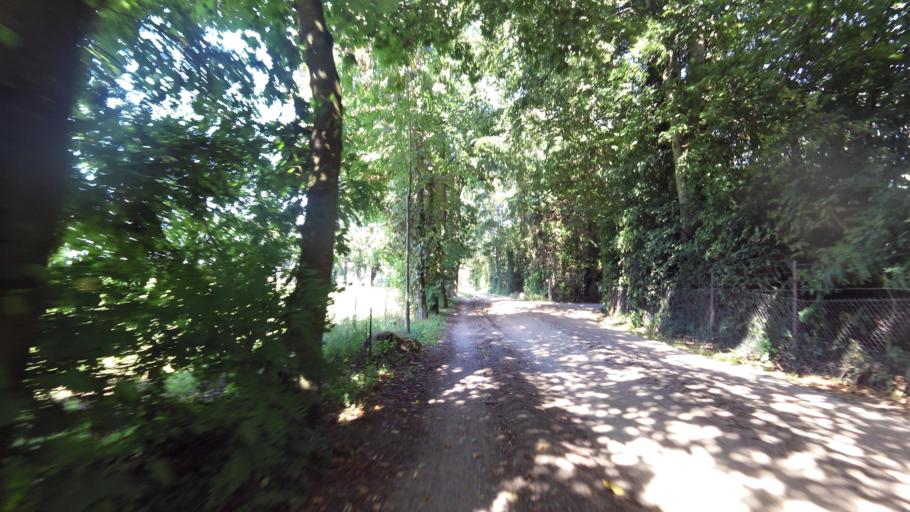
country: NL
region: Gelderland
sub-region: Gemeente Ede
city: Harskamp
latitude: 52.1311
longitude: 5.7648
